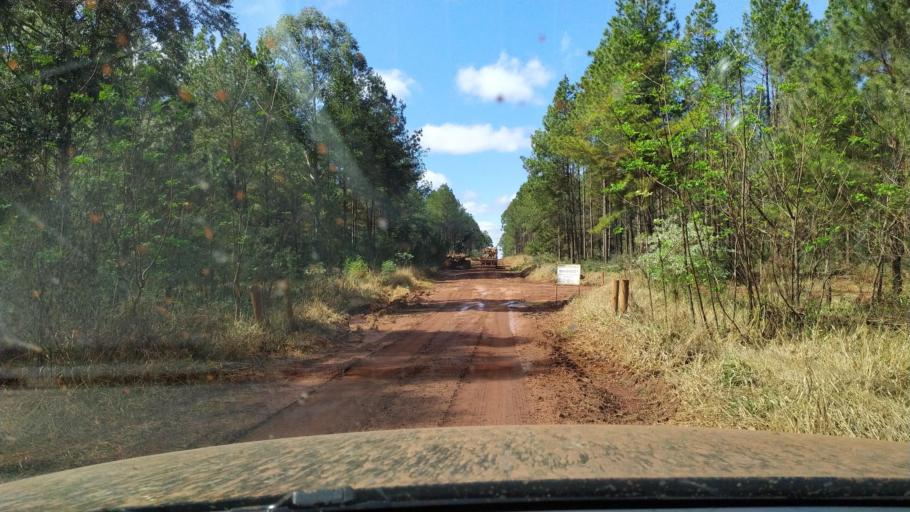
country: AR
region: Corrientes
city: Santo Tome
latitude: -28.4030
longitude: -56.0131
